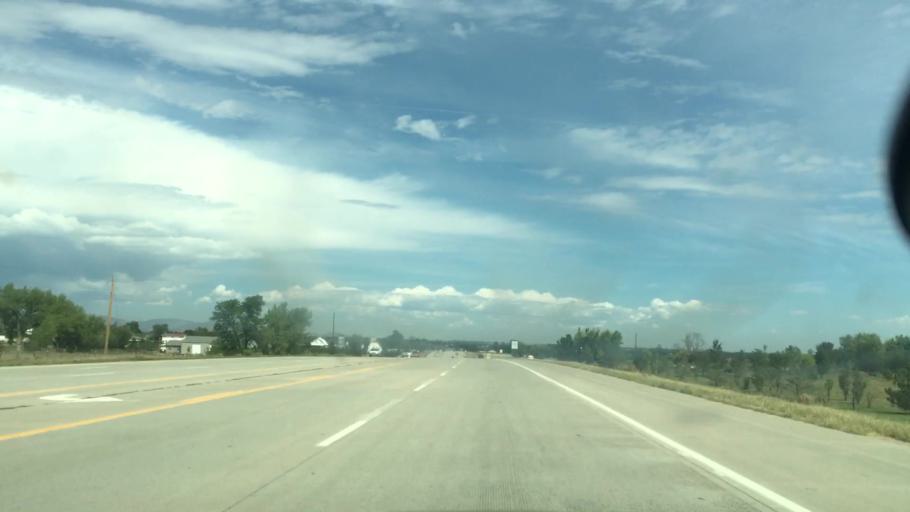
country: US
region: Colorado
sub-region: Larimer County
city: Berthoud
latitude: 40.2584
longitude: -105.1025
